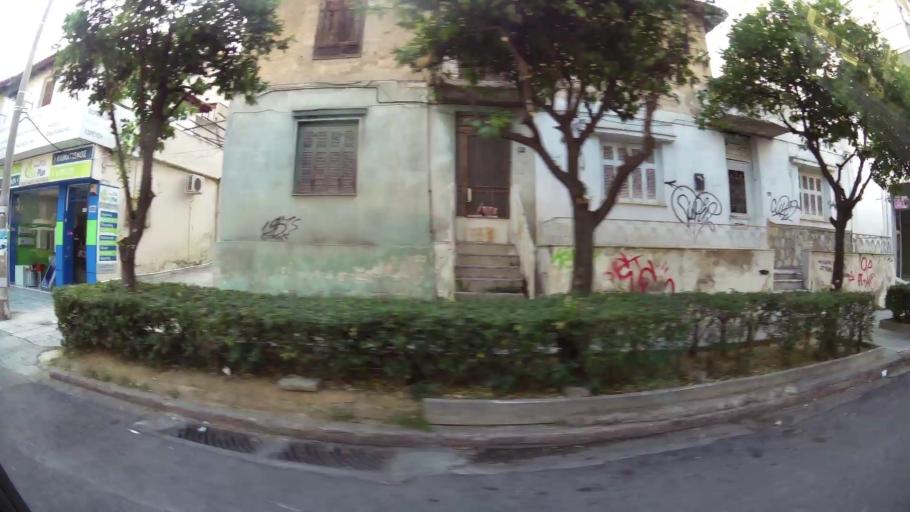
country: GR
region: Attica
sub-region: Nomarchia Athinas
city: Nea Ionia
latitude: 38.0461
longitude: 23.7511
